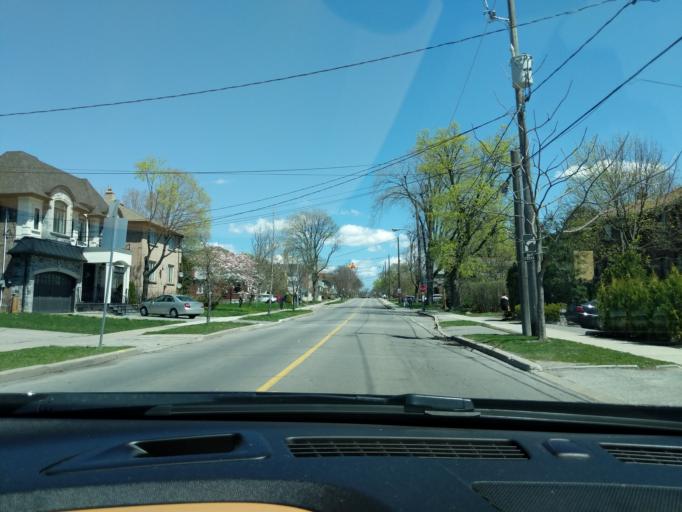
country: CA
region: Ontario
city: Toronto
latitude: 43.7112
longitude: -79.4336
